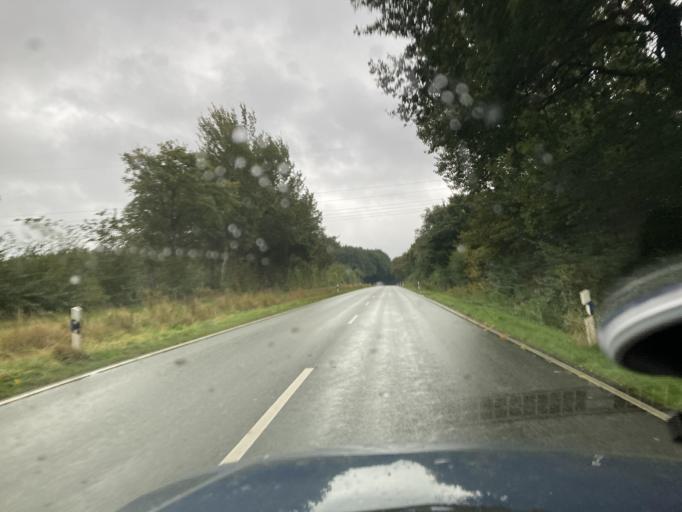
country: DE
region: Schleswig-Holstein
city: Ostrohe
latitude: 54.1962
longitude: 9.1687
